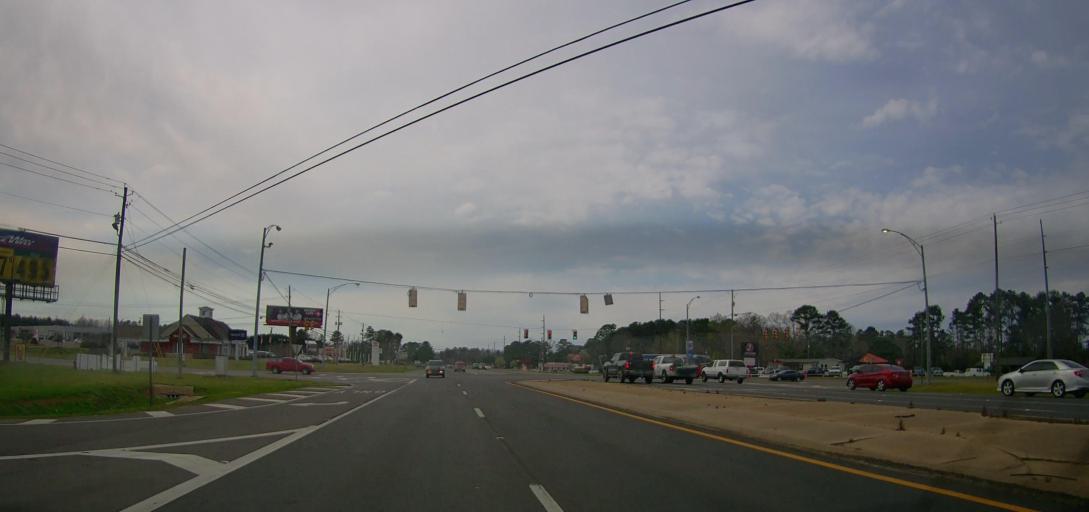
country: US
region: Alabama
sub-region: Walker County
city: Jasper
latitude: 33.8383
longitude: -87.2300
